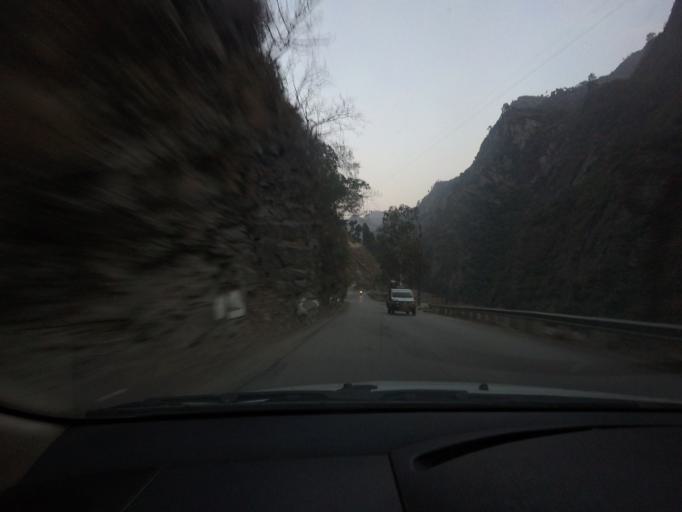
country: IN
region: Himachal Pradesh
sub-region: Mandi
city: Pandoh
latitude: 31.6952
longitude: 77.1432
